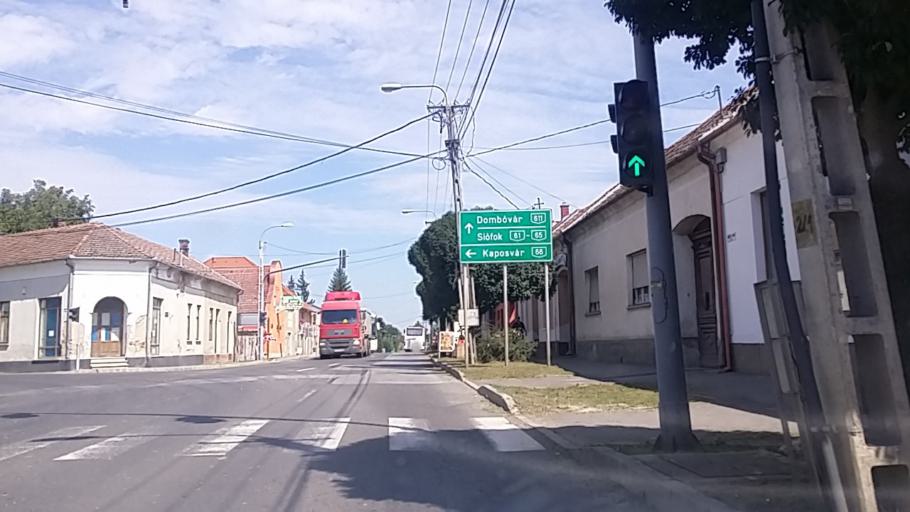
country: HU
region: Baranya
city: Sasd
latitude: 46.2545
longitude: 18.1061
